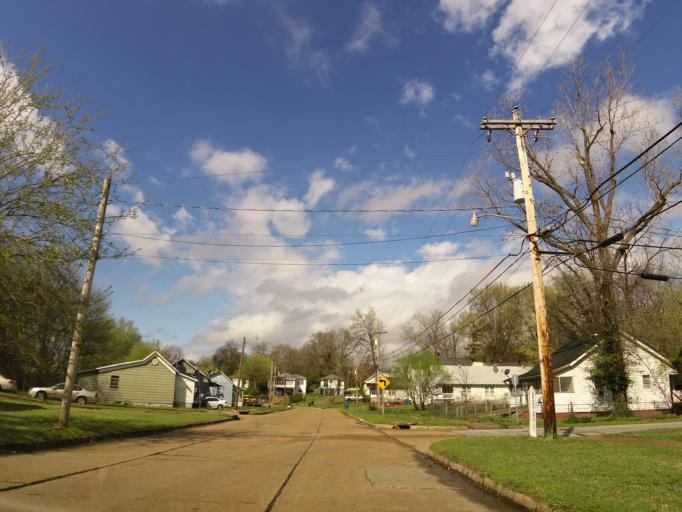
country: US
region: Missouri
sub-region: Butler County
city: Poplar Bluff
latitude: 36.7623
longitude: -90.3915
